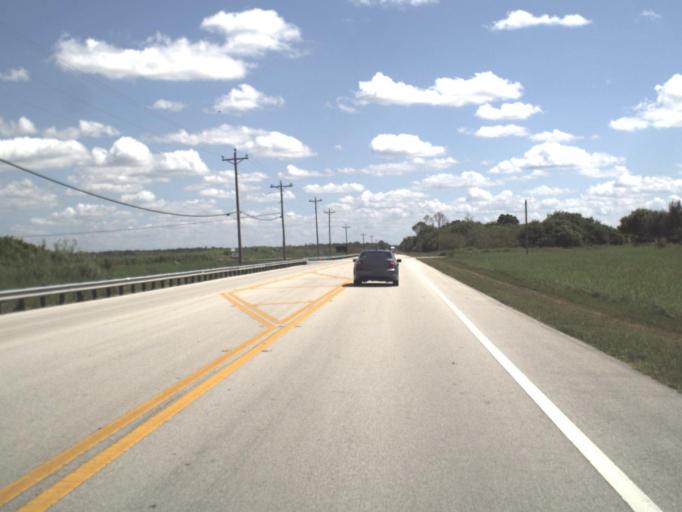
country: US
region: Florida
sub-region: Collier County
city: Lely Resort
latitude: 26.0149
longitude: -81.6237
